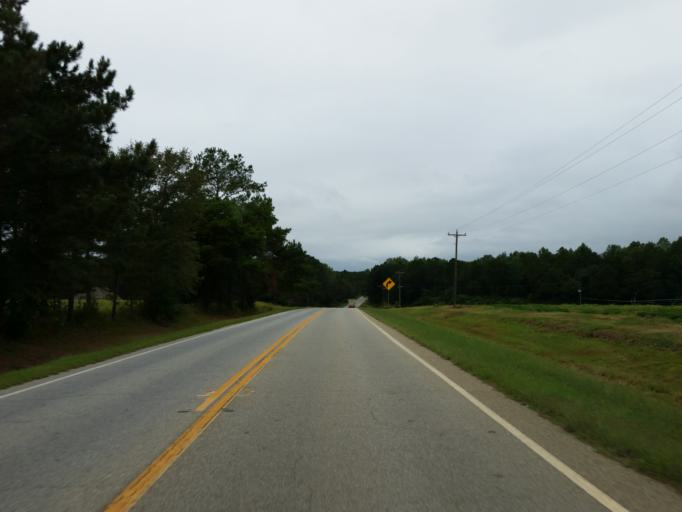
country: US
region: Georgia
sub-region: Cook County
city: Adel
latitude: 31.1312
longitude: -83.3619
